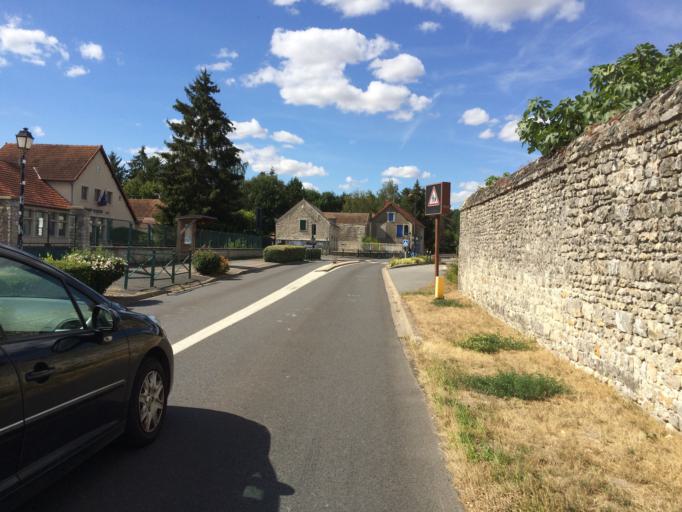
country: FR
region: Ile-de-France
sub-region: Departement de l'Essonne
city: Boutigny-sur-Essonne
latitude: 48.4374
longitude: 2.3542
